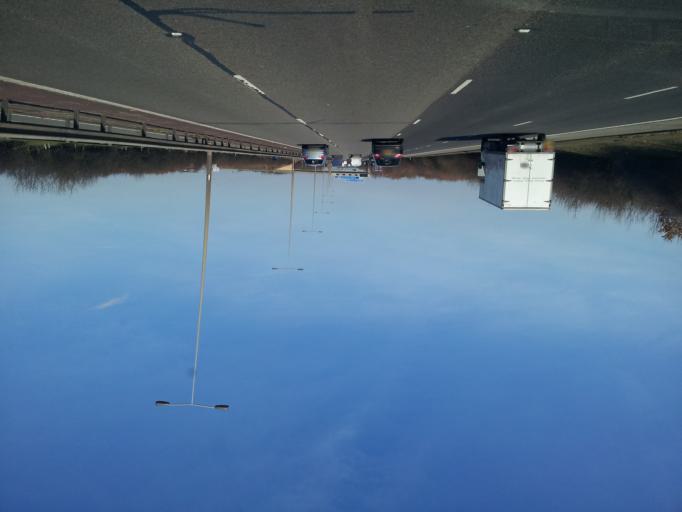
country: GB
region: England
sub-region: Cambridgeshire
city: Sawtry
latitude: 52.4187
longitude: -0.2679
